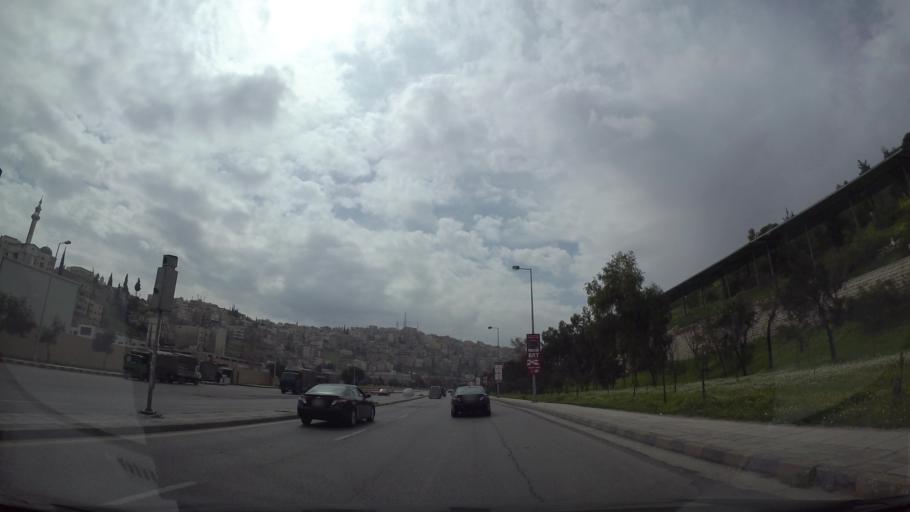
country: JO
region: Amman
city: Amman
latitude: 31.9579
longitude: 35.9544
